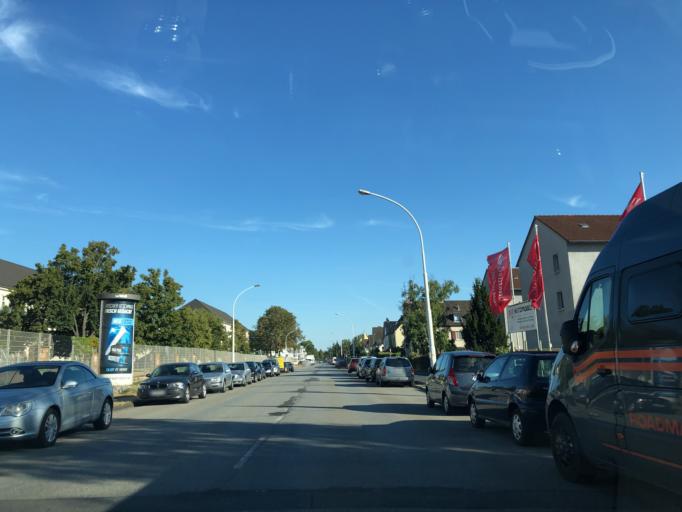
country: DE
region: Rheinland-Pfalz
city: Mainz
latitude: 50.0212
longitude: 8.2707
